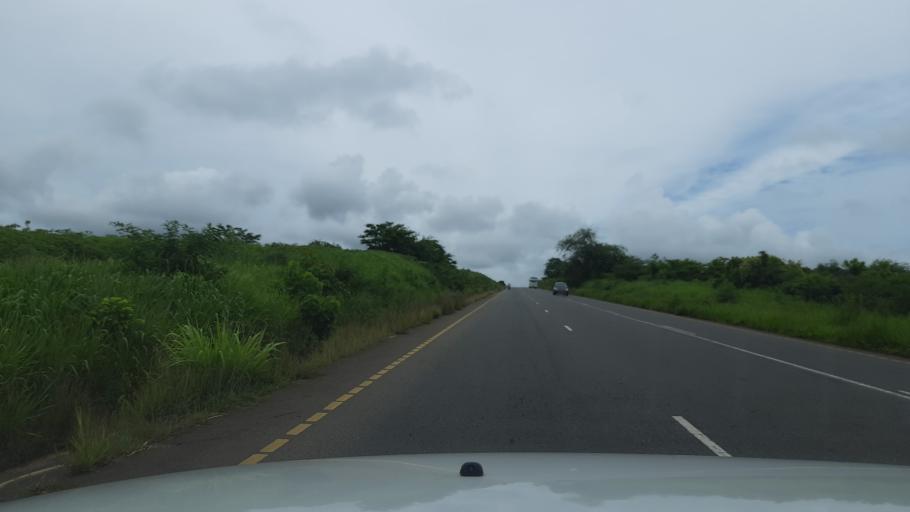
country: TZ
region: Pwani
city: Lugoba
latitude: -6.0393
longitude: 38.2405
